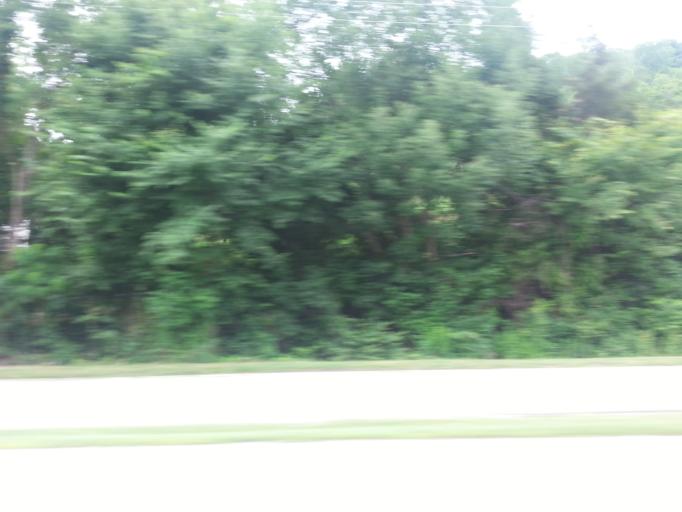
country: US
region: Ohio
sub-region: Brown County
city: Ripley
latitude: 38.7233
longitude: -83.8291
